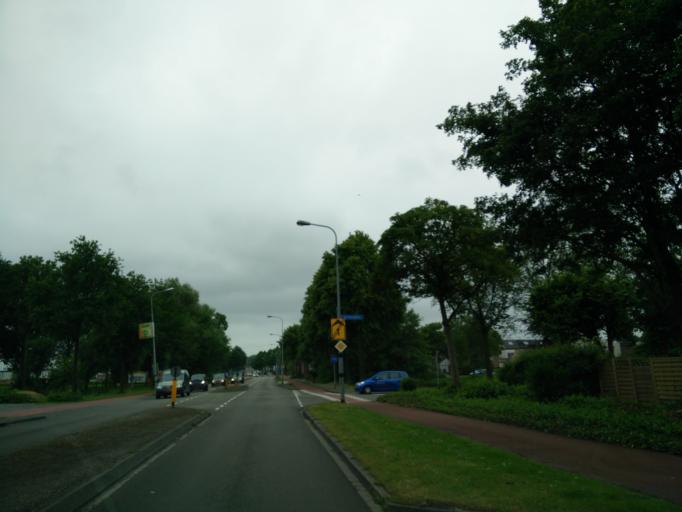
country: NL
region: Groningen
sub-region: Gemeente Groningen
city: Groningen
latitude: 53.2073
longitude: 6.5071
